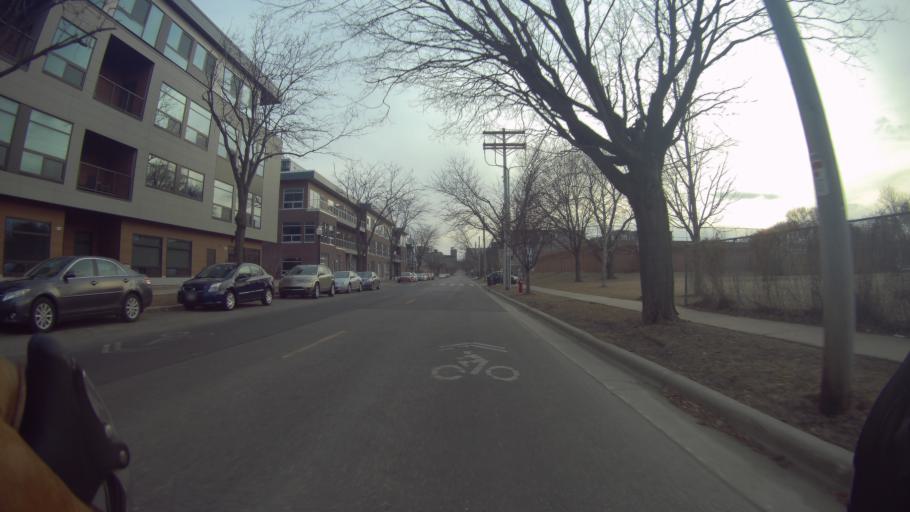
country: US
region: Wisconsin
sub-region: Dane County
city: Madison
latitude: 43.0826
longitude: -89.3750
